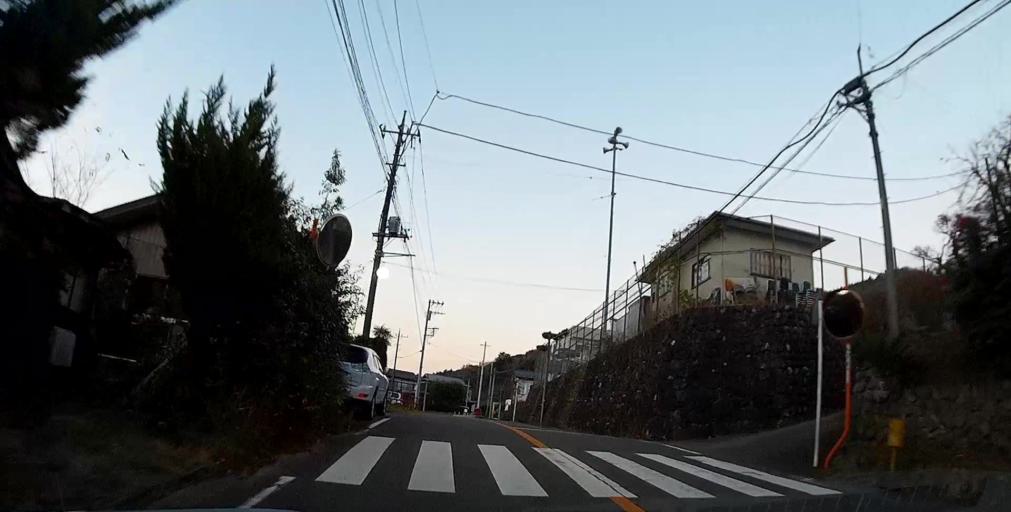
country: JP
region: Yamanashi
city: Uenohara
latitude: 35.5886
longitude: 139.1733
